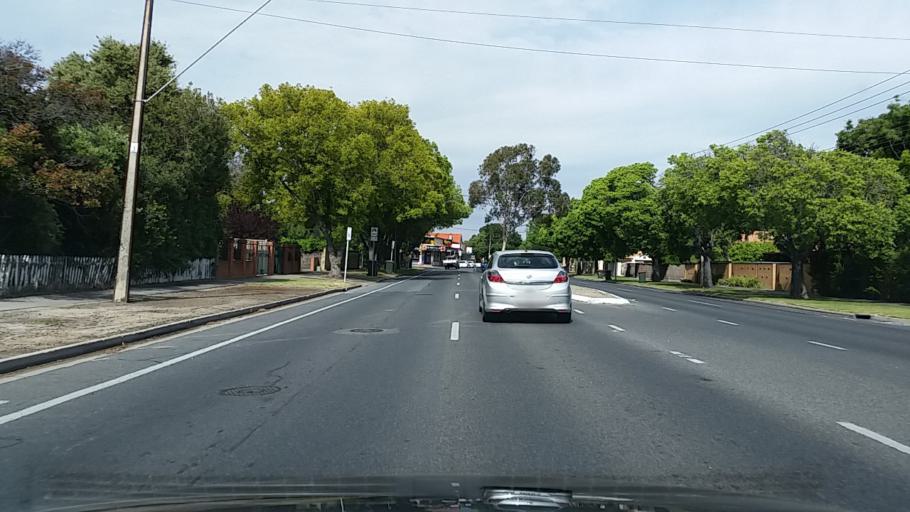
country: AU
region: South Australia
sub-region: Charles Sturt
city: Findon
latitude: -34.9260
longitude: 138.5277
